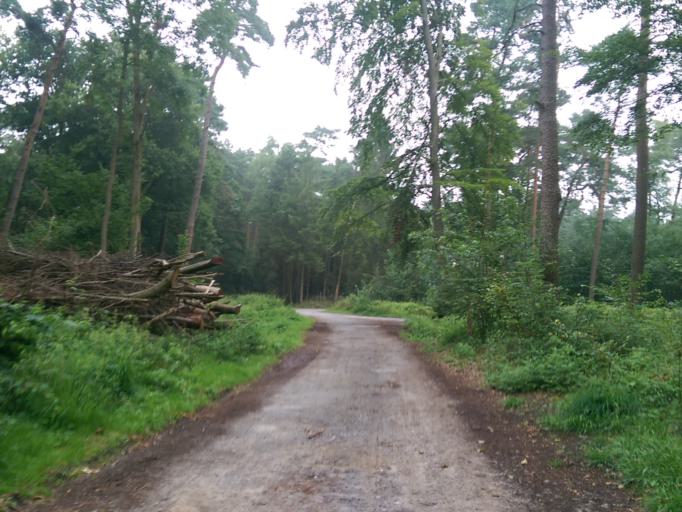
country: DE
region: North Rhine-Westphalia
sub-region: Regierungsbezirk Detmold
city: Rheda-Wiedenbruck
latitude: 51.8932
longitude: 8.3219
